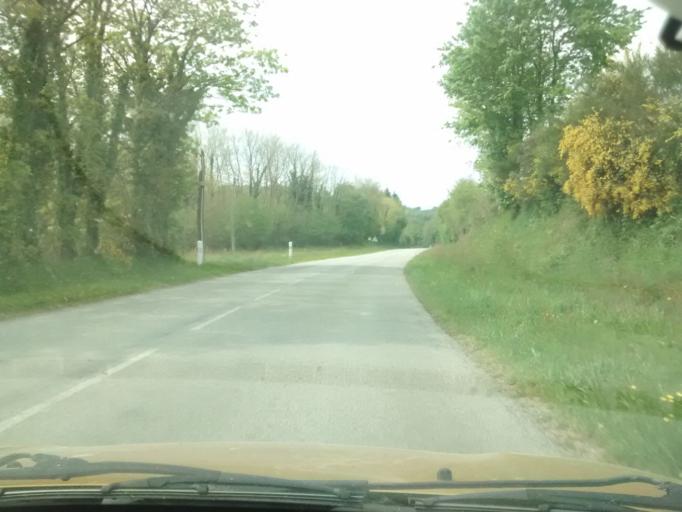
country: FR
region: Brittany
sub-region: Departement du Morbihan
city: Questembert
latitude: 47.6526
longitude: -2.4839
